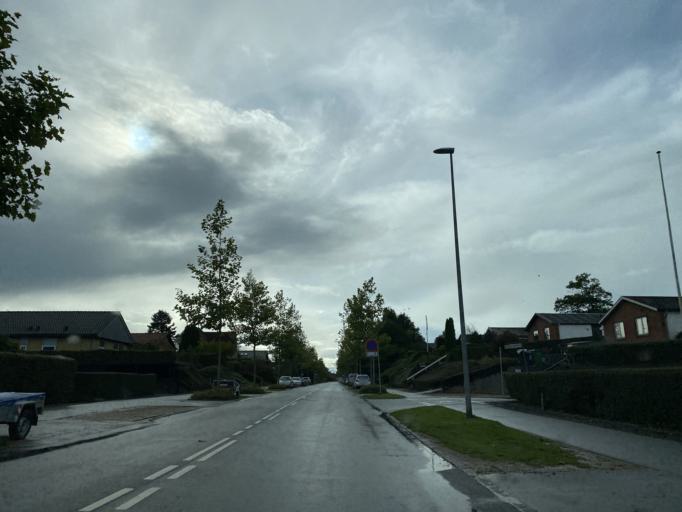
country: DK
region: South Denmark
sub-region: Haderslev Kommune
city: Haderslev
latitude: 55.2550
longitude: 9.4642
